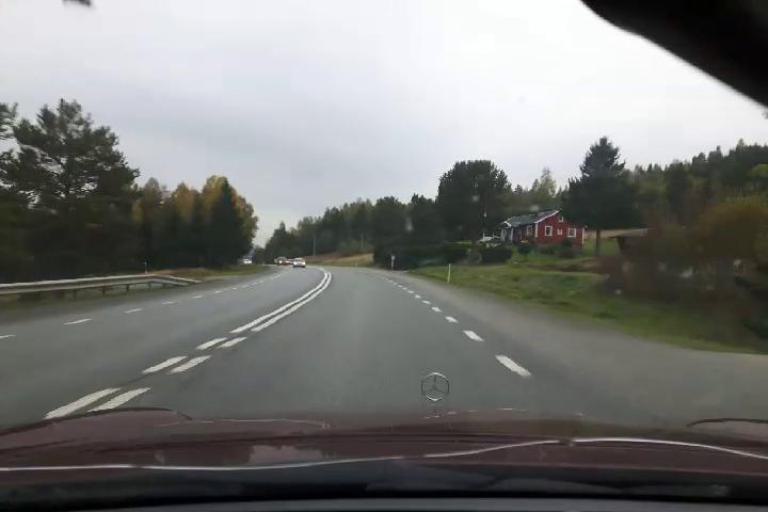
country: SE
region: Vaesternorrland
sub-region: Kramfors Kommun
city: Nordingra
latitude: 63.0091
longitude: 18.2899
